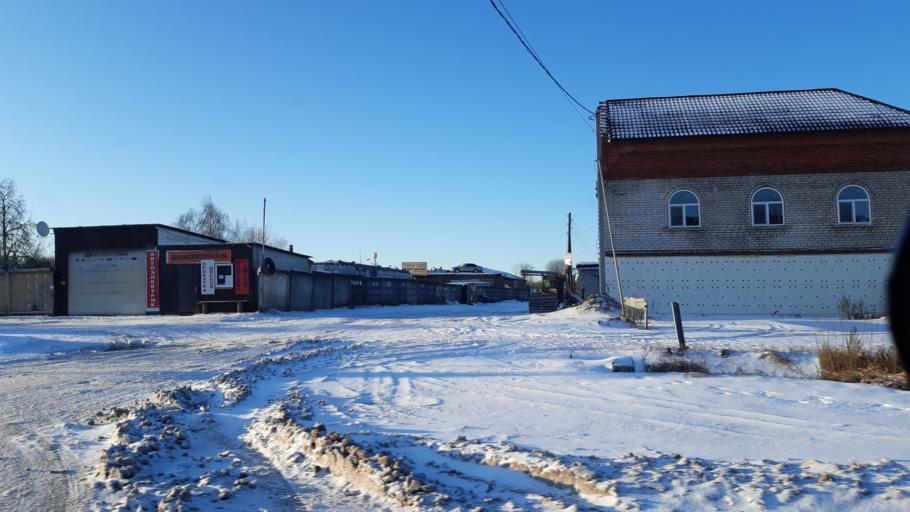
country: RU
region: Moskovskaya
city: Skoropuskovskiy
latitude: 56.3422
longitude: 38.1672
